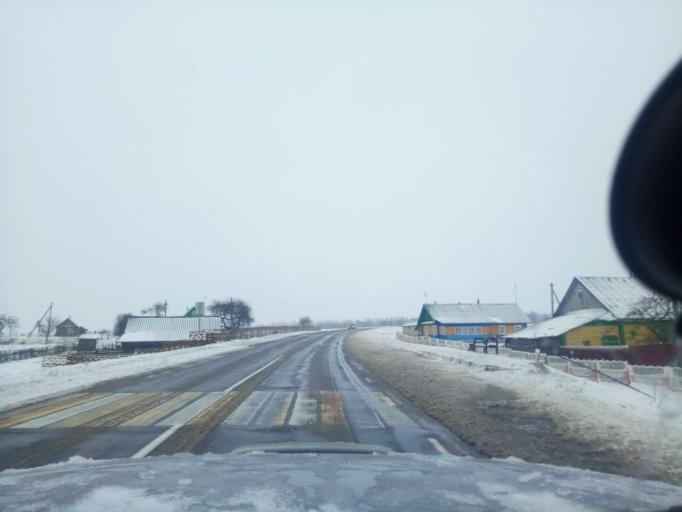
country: BY
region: Minsk
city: Haradzyeya
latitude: 53.3329
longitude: 26.5411
